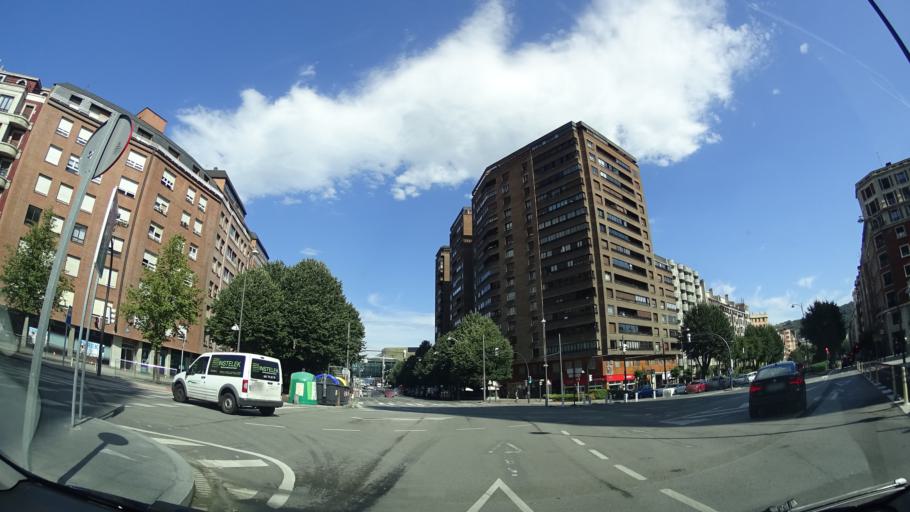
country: ES
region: Basque Country
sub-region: Bizkaia
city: Bilbao
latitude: 43.2605
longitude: -2.9470
